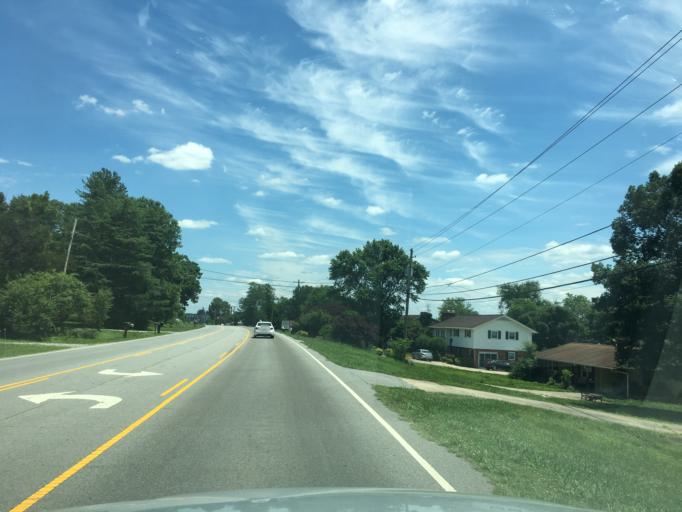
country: US
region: North Carolina
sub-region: Burke County
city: Glen Alpine
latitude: 35.7246
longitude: -81.7436
